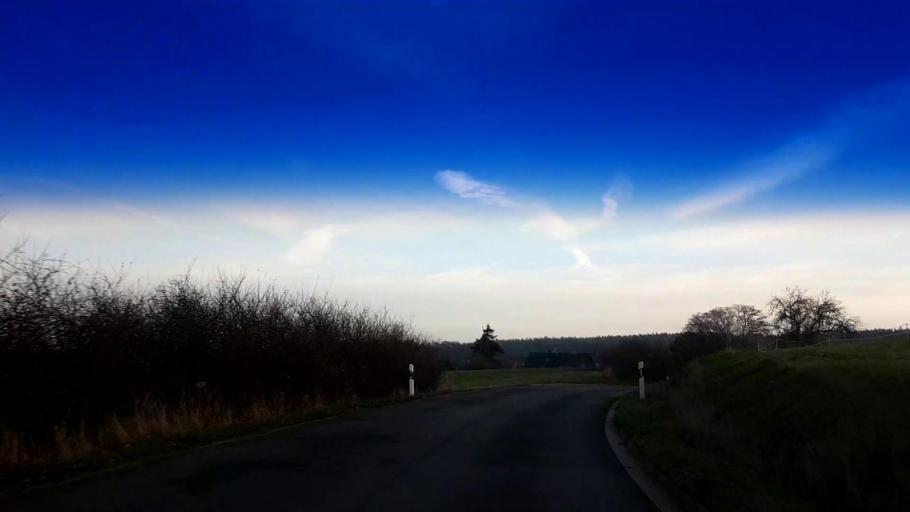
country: DE
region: Bavaria
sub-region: Upper Franconia
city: Stegaurach
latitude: 49.8617
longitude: 10.8220
